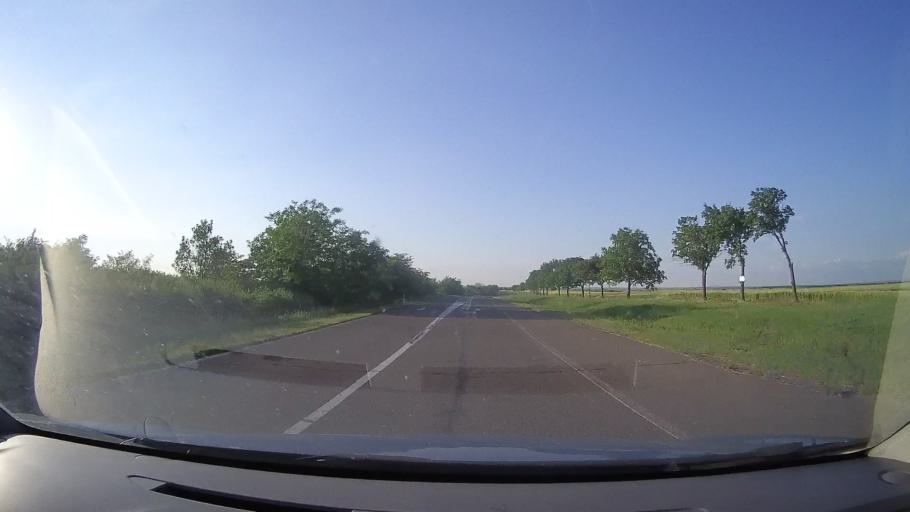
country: RO
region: Timis
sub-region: Comuna Moravita
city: Moravita
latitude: 45.2095
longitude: 21.2998
